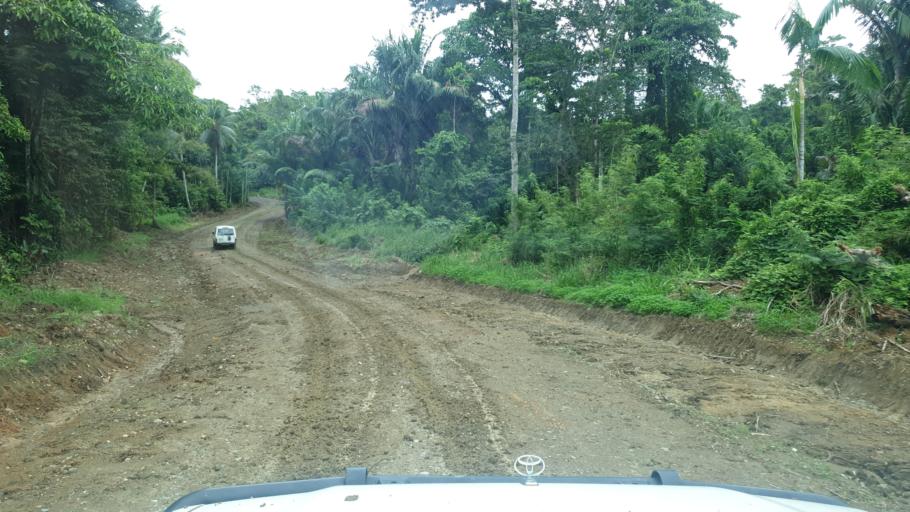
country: PG
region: Gulf
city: Kerema
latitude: -7.9594
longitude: 145.8407
